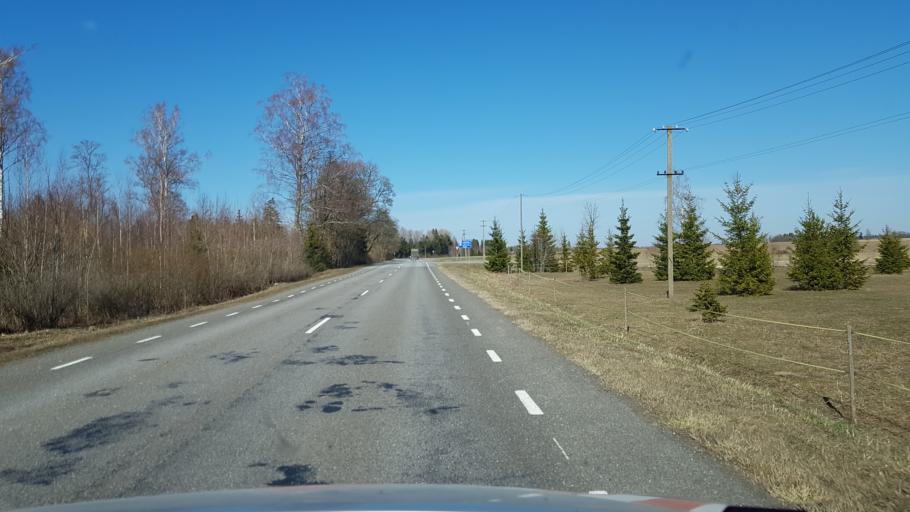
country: EE
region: Jaervamaa
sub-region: Jaerva-Jaani vald
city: Jarva-Jaani
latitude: 59.0657
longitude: 25.9319
